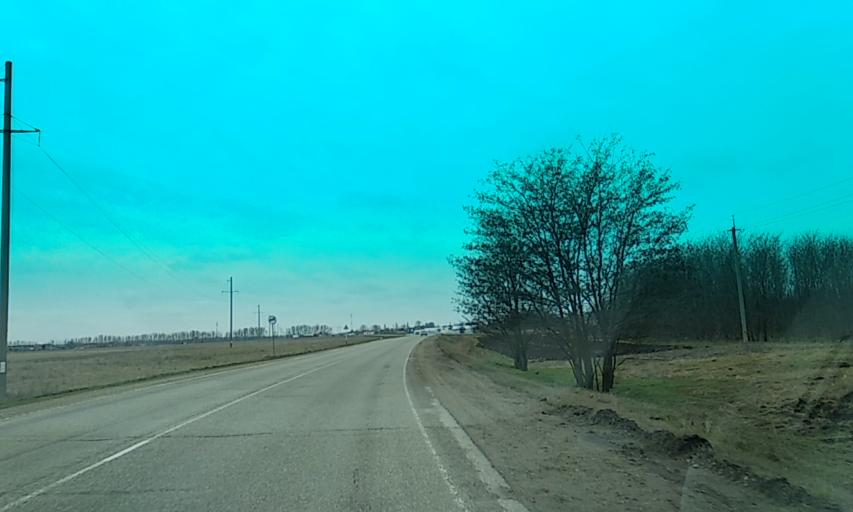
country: RU
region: Krasnodarskiy
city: Dvubratskiy
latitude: 45.3707
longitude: 39.7119
